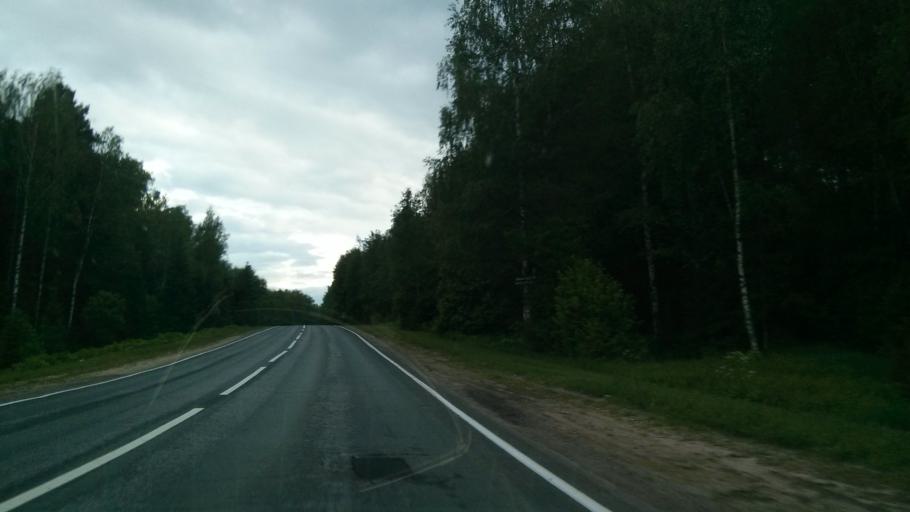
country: RU
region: Nizjnij Novgorod
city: Vacha
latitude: 55.7651
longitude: 42.5336
